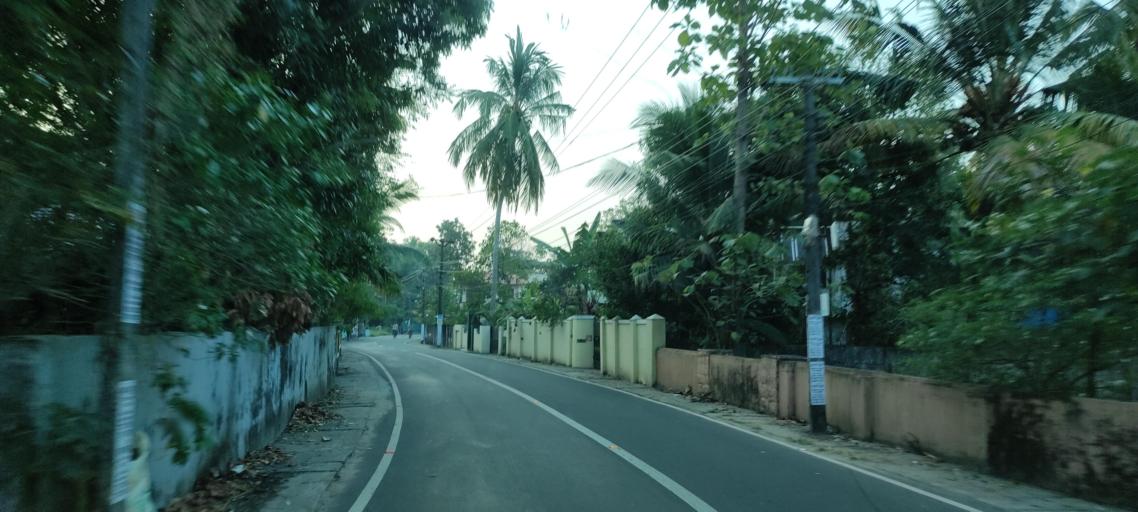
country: IN
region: Kerala
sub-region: Alappuzha
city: Alleppey
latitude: 9.4644
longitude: 76.3431
